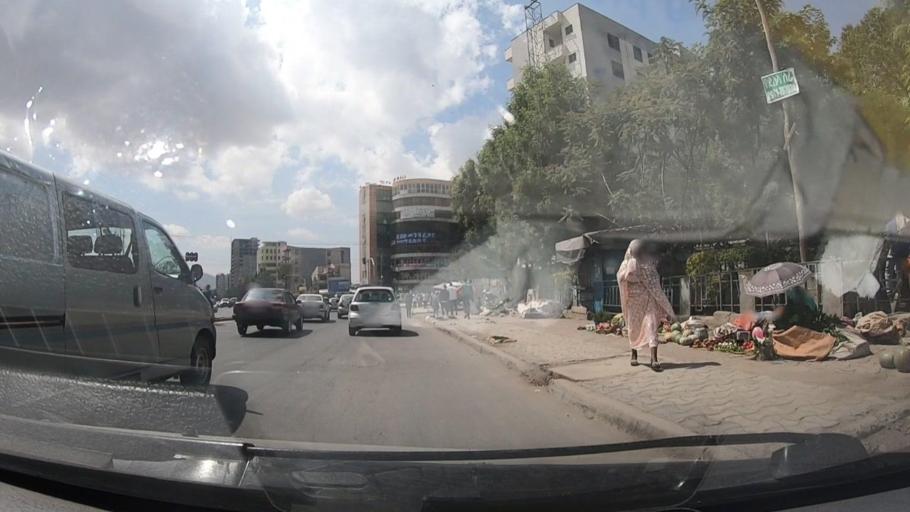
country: ET
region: Adis Abeba
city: Addis Ababa
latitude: 8.9694
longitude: 38.7224
